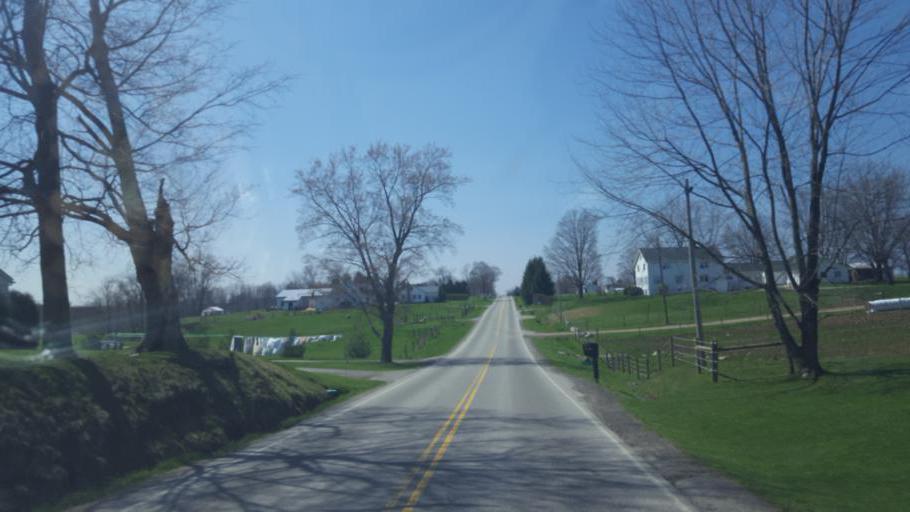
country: US
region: Ohio
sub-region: Portage County
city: Hiram
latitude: 41.3870
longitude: -81.1133
